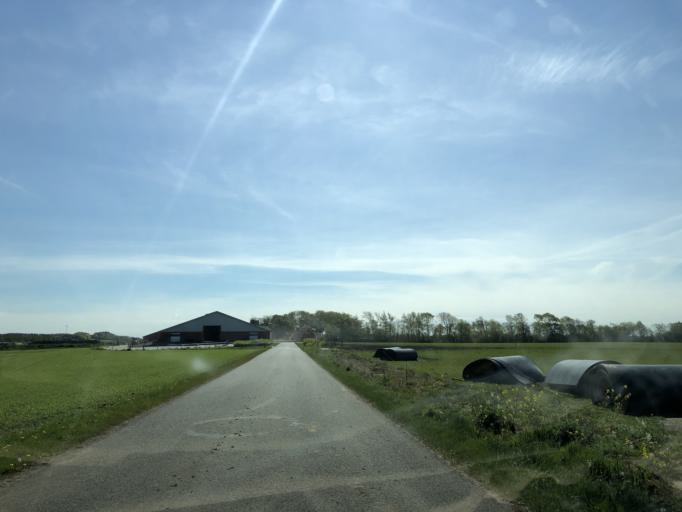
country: DK
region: Central Jutland
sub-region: Ringkobing-Skjern Kommune
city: Videbaek
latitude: 56.1929
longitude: 8.5124
